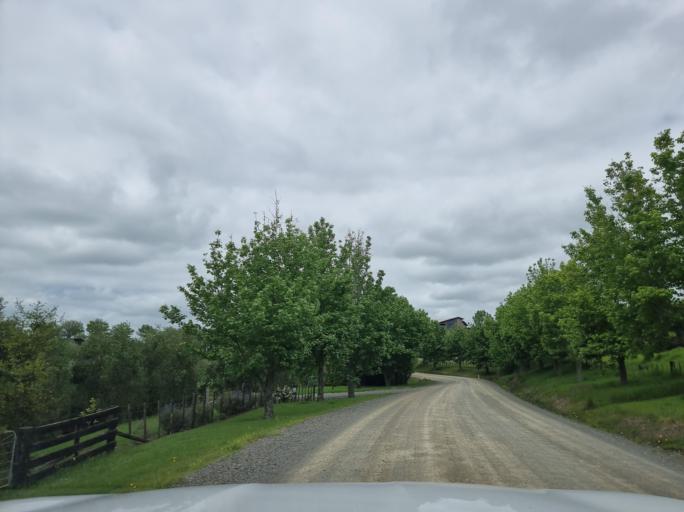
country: NZ
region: Auckland
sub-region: Auckland
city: Wellsford
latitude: -36.0907
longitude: 174.5300
